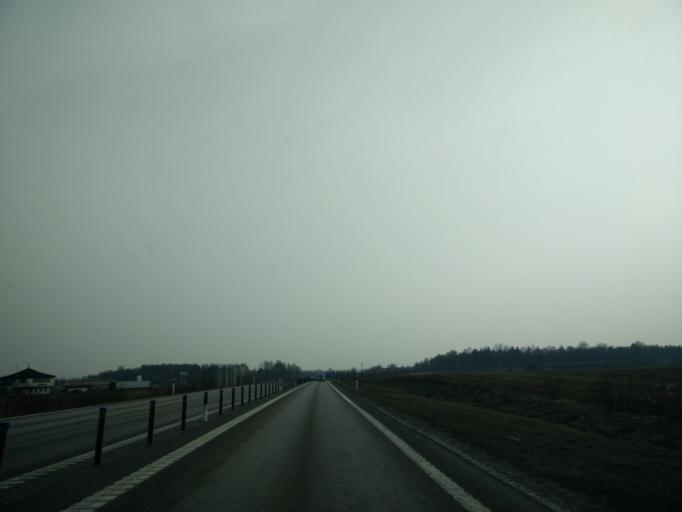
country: SE
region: Vaermland
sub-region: Karlstads Kommun
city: Karlstad
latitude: 59.4332
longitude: 13.4127
